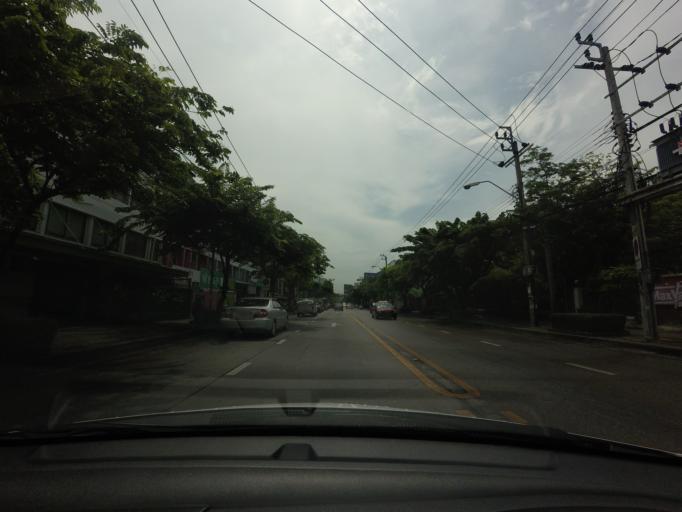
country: TH
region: Bangkok
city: Phra Khanong
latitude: 13.7106
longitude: 100.6114
